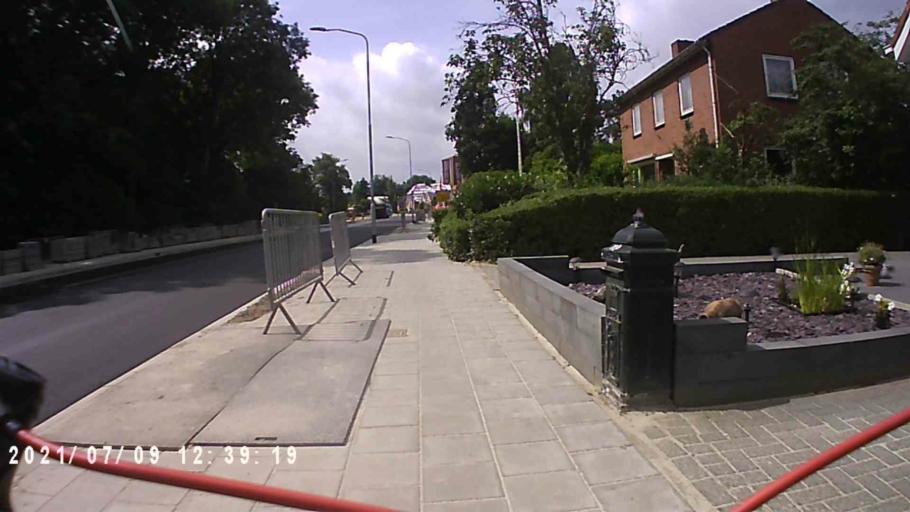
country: NL
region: Groningen
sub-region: Gemeente  Oldambt
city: Winschoten
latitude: 53.1413
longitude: 7.0216
